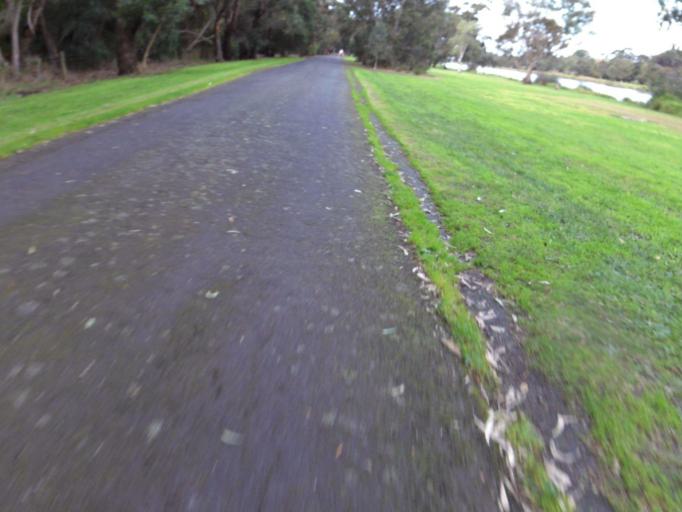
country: AU
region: Victoria
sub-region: Greater Geelong
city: Geelong West
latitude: -38.1632
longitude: 144.3404
